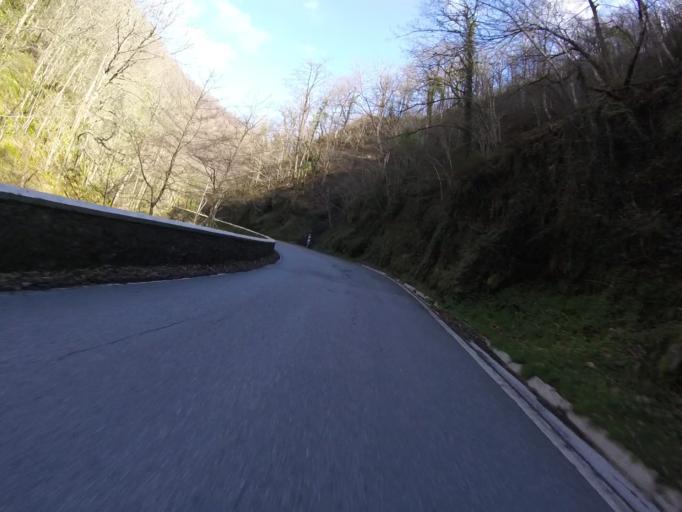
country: ES
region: Navarre
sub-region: Provincia de Navarra
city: Ezkurra
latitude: 43.1146
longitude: -1.8538
